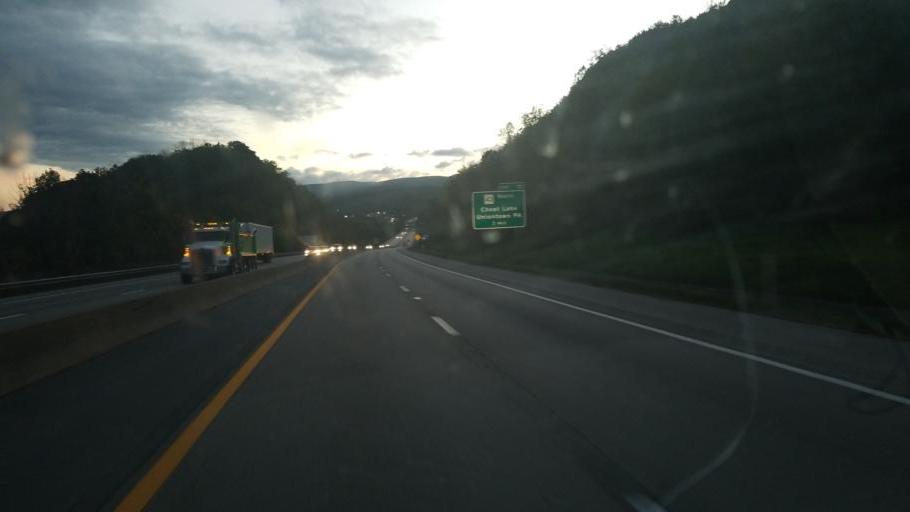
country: US
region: West Virginia
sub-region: Monongalia County
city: Cheat Lake
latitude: 39.6661
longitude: -79.8724
